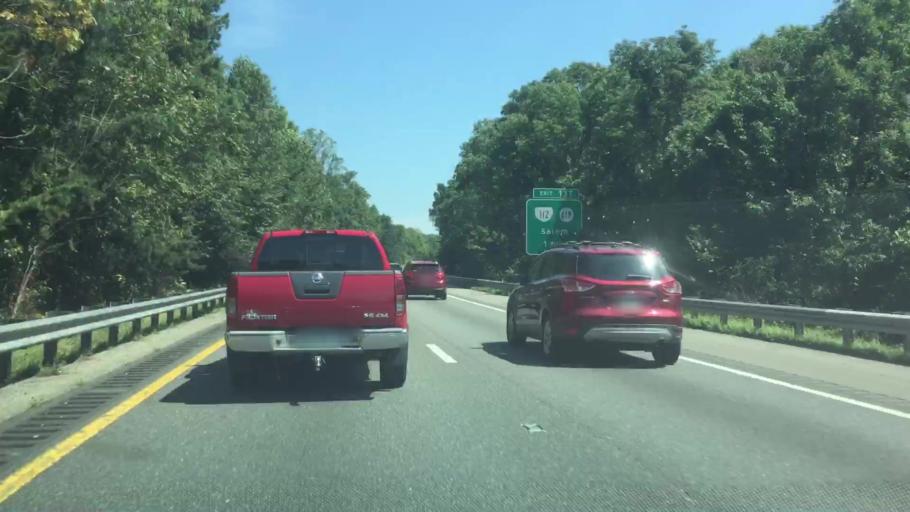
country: US
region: Virginia
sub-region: City of Salem
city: Salem
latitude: 37.2867
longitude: -80.1200
